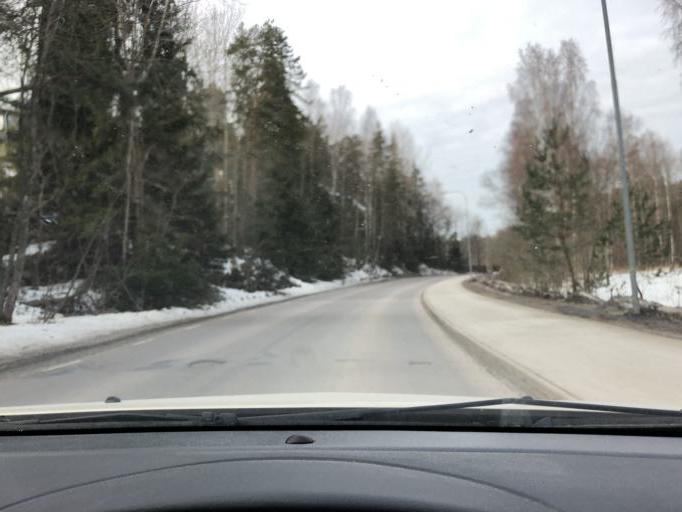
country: SE
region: Stockholm
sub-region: Nacka Kommun
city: Boo
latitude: 59.3323
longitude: 18.3120
